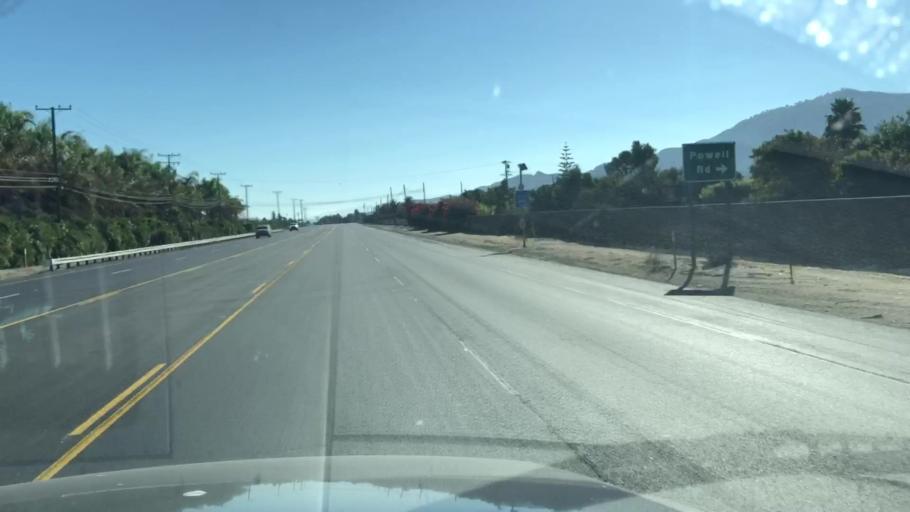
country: US
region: California
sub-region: Ventura County
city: Piru
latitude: 34.4007
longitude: -118.8162
